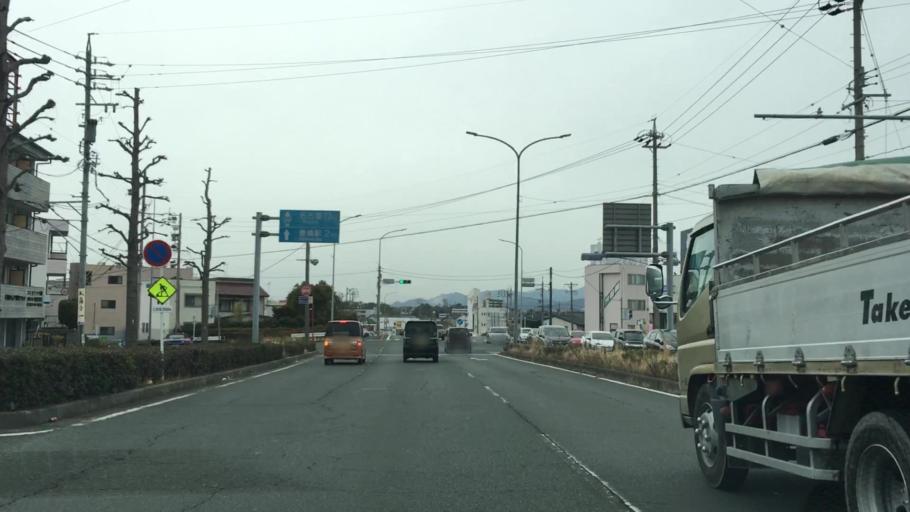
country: JP
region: Aichi
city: Toyohashi
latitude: 34.7455
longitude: 137.3865
